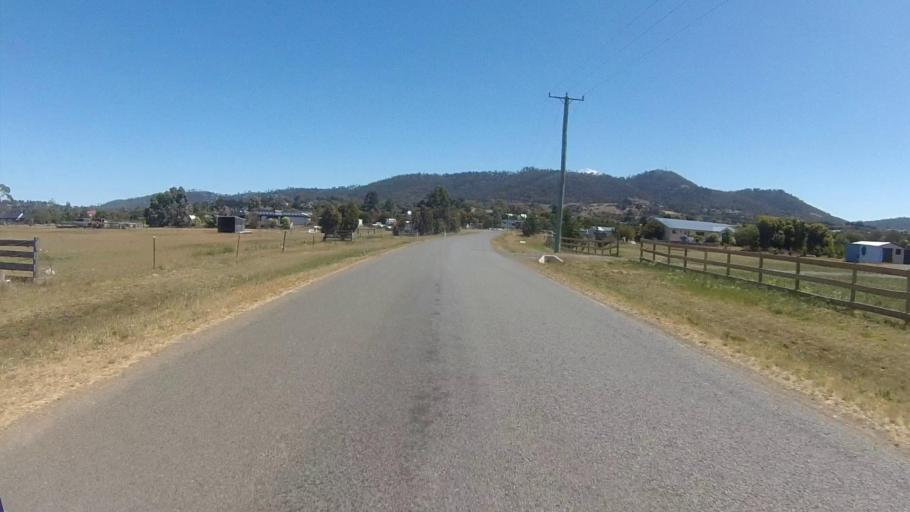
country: AU
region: Tasmania
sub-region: Clarence
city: Seven Mile Beach
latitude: -42.8529
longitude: 147.4900
